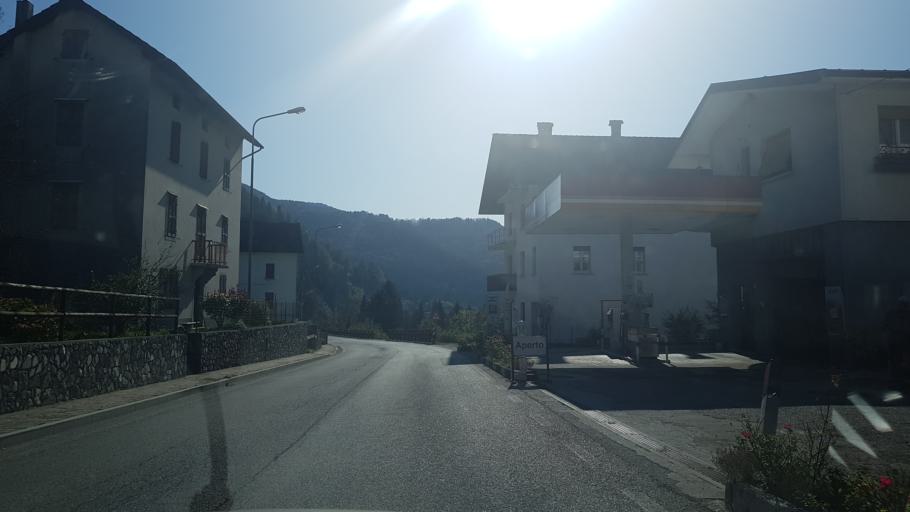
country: IT
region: Friuli Venezia Giulia
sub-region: Provincia di Udine
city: Ovaro
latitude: 46.4794
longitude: 12.8676
